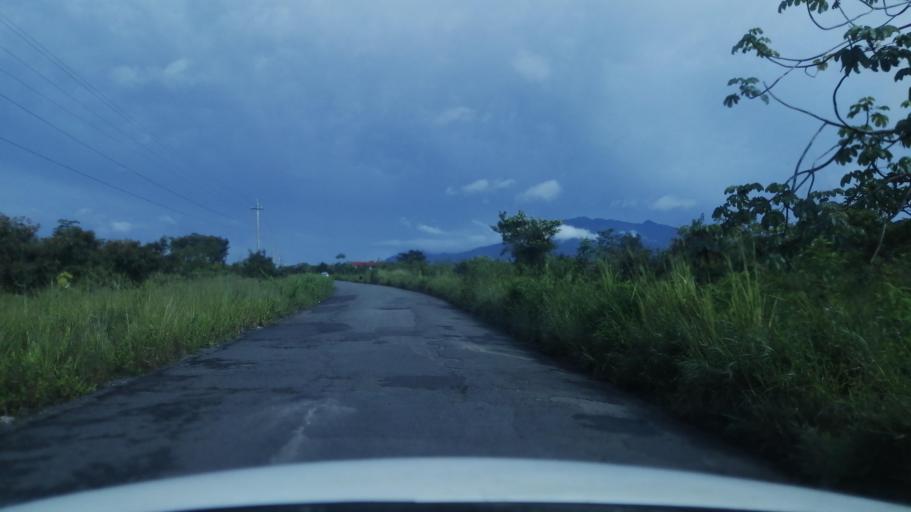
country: PA
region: Chiriqui
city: Potrerillos Abajo
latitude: 8.6686
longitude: -82.4308
